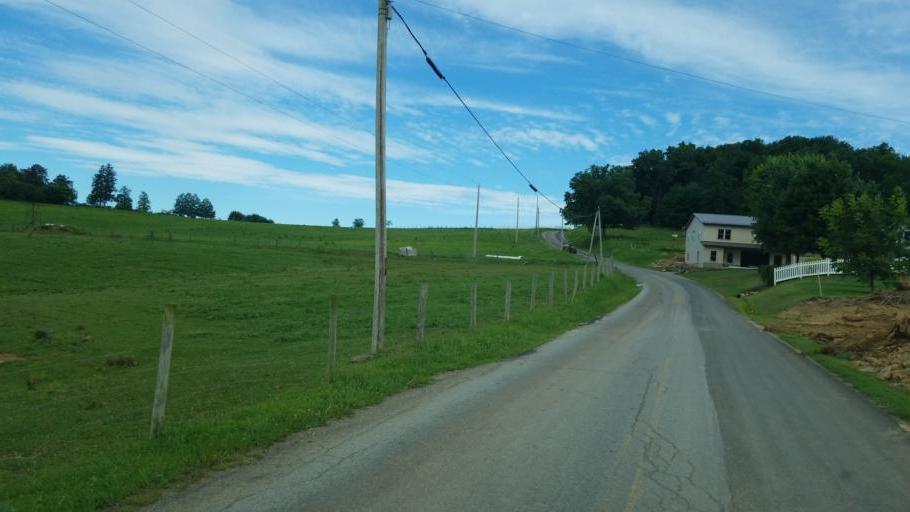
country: US
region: Ohio
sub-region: Holmes County
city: Millersburg
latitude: 40.5130
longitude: -81.8362
